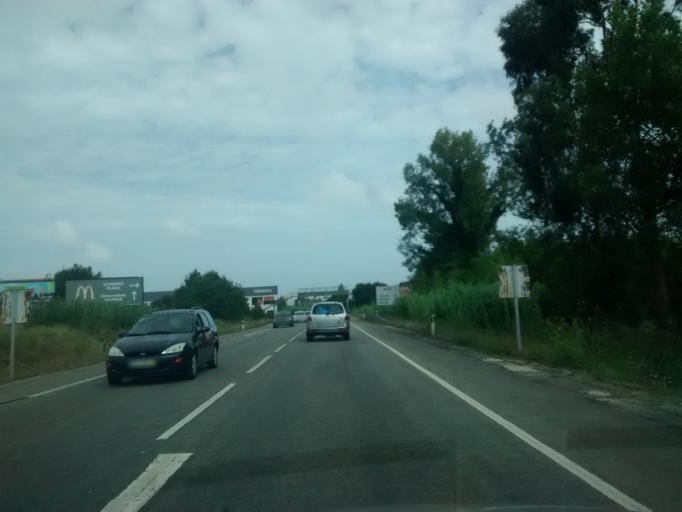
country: PT
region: Aveiro
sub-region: Aveiro
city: Aradas
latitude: 40.6133
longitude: -8.6336
